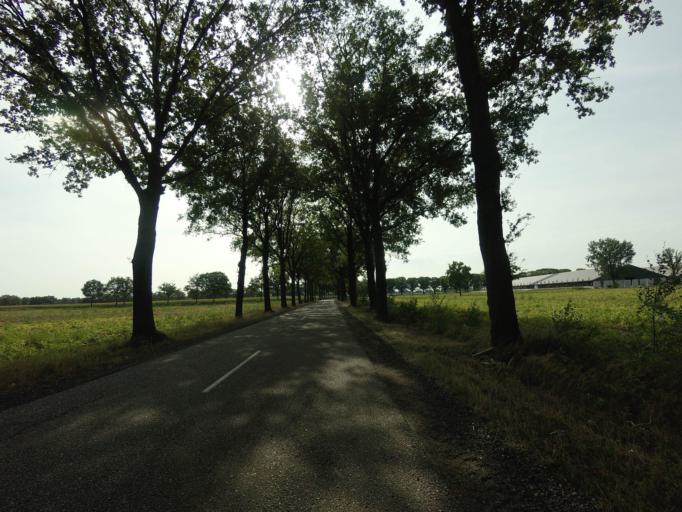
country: NL
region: North Brabant
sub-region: Gemeente Sint Anthonis
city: Sint Anthonis
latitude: 51.5946
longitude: 5.8406
